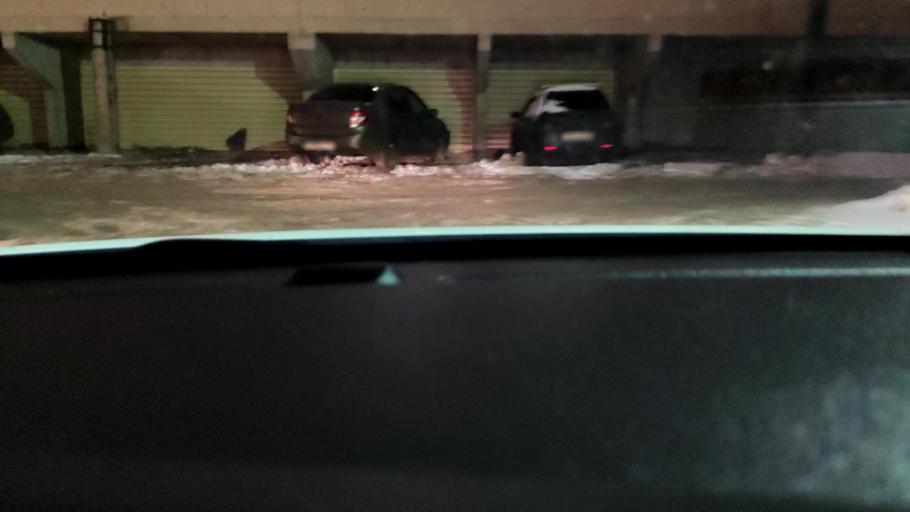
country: RU
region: Tatarstan
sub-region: Gorod Kazan'
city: Kazan
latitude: 55.8350
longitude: 49.0569
